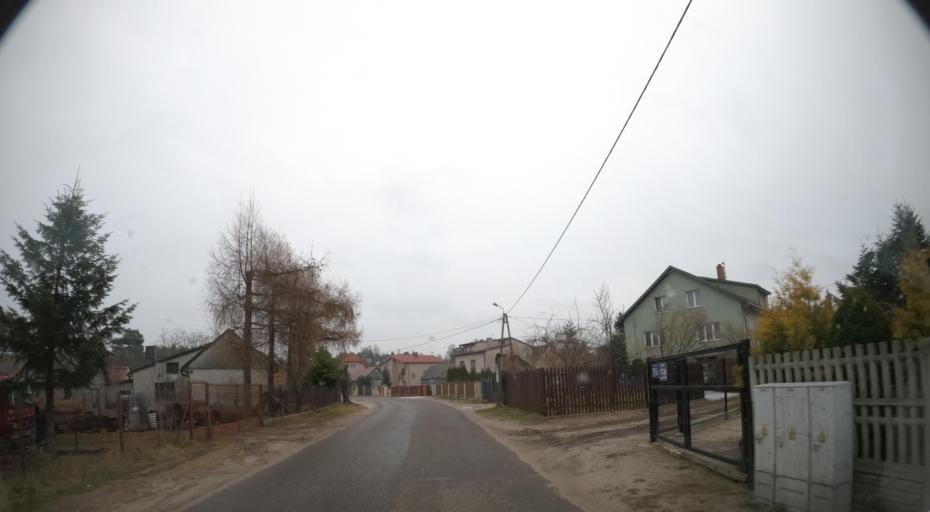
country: PL
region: Masovian Voivodeship
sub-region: Powiat radomski
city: Jedlnia-Letnisko
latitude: 51.4147
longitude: 21.2563
